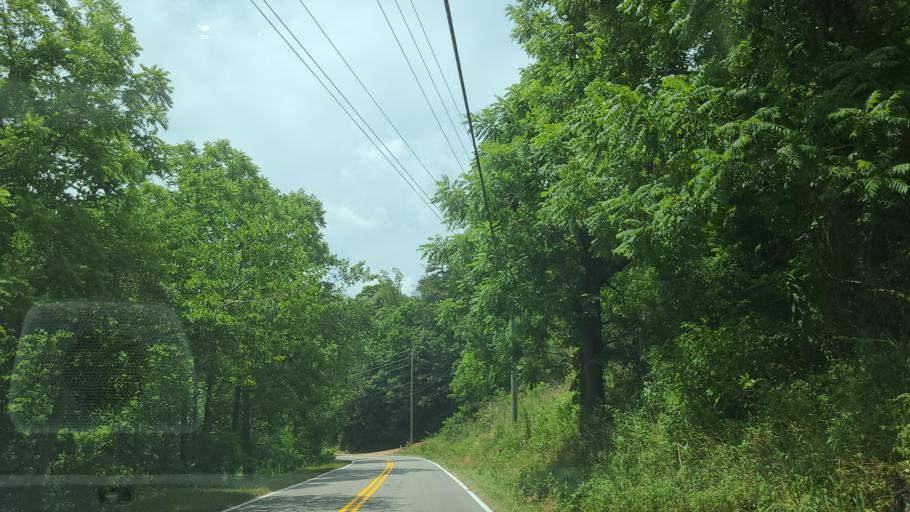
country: US
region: North Carolina
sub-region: Buncombe County
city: Avery Creek
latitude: 35.4890
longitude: -82.5742
